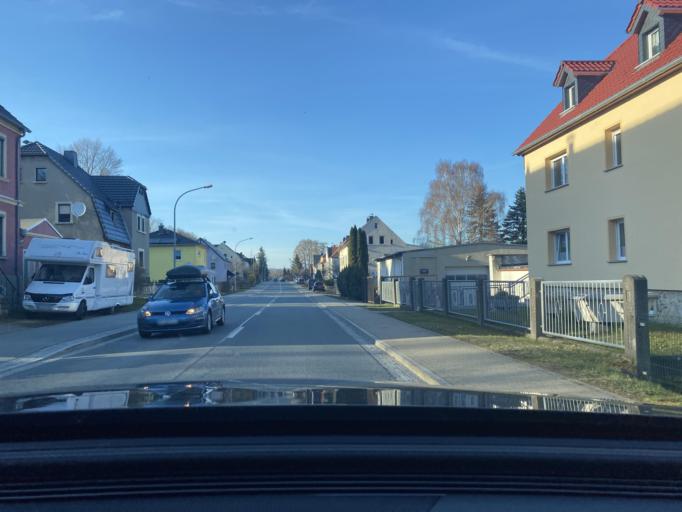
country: DE
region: Saxony
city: Schirgiswalde
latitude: 51.0651
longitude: 14.4296
